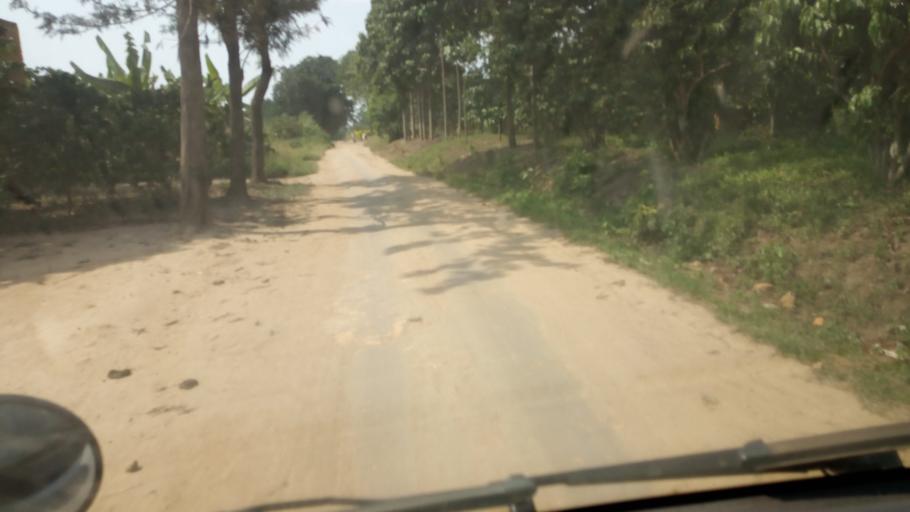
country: UG
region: Western Region
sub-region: Kanungu District
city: Ntungamo
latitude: -0.7884
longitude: 29.6880
